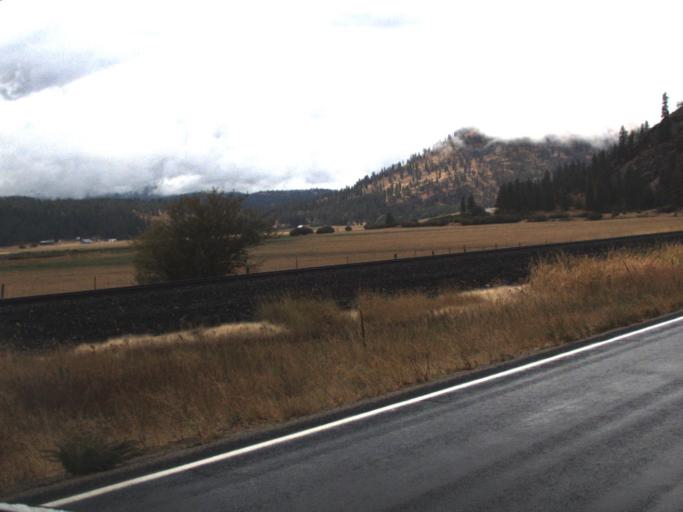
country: US
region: Washington
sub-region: Stevens County
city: Chewelah
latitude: 48.1877
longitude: -117.7324
